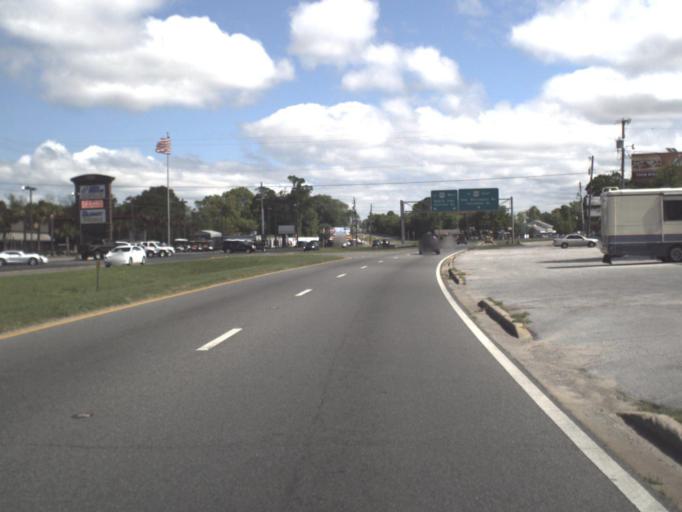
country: US
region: Florida
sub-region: Escambia County
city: West Pensacola
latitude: 30.4201
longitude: -87.2753
